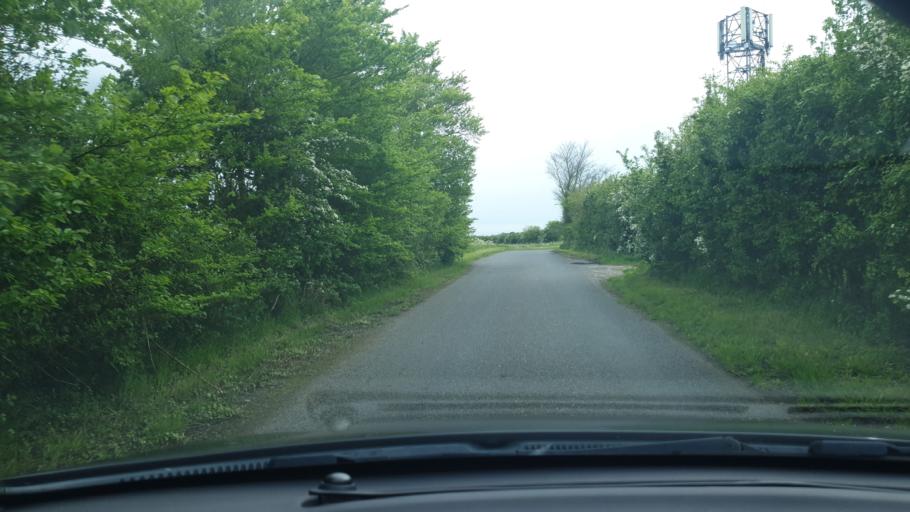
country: GB
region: England
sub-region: Essex
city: Mistley
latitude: 51.9172
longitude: 1.1654
